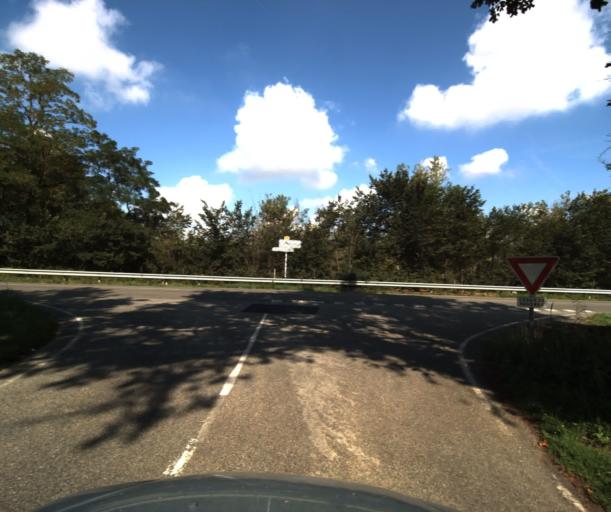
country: FR
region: Midi-Pyrenees
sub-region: Departement de la Haute-Garonne
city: Portet-sur-Garonne
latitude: 43.5159
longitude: 1.4174
